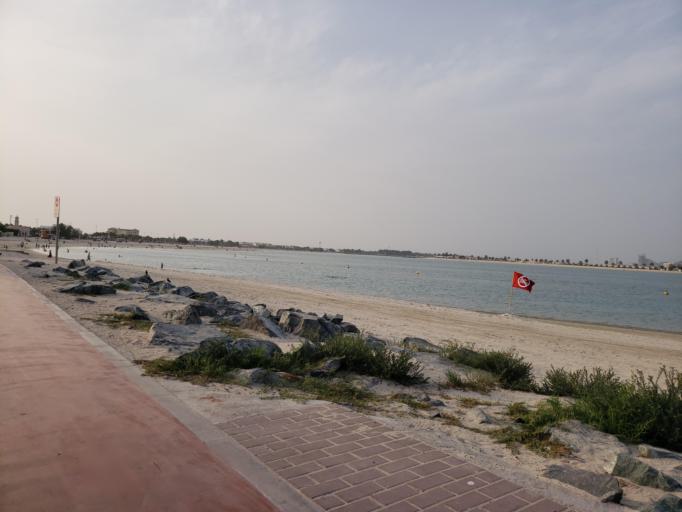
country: AE
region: Ash Shariqah
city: Sharjah
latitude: 25.2981
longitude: 55.3525
